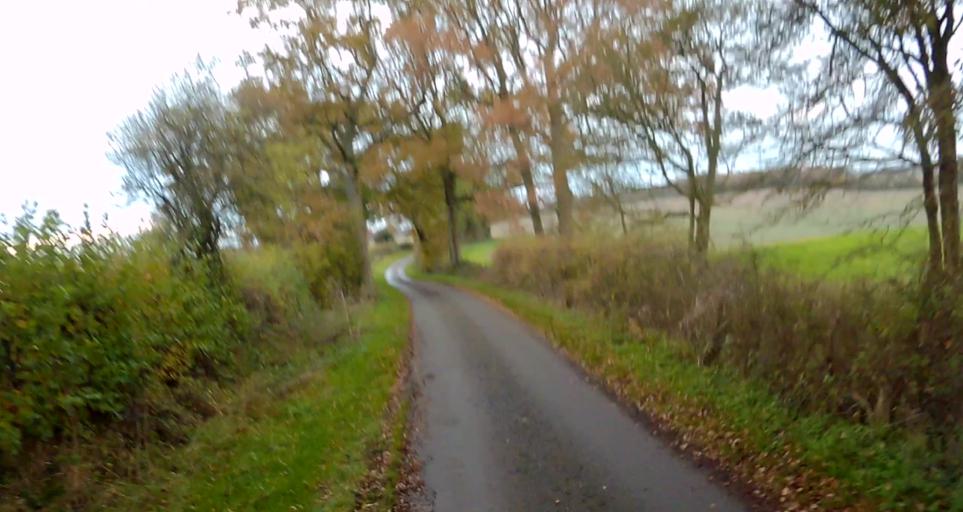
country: GB
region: England
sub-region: Hampshire
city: Long Sutton
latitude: 51.2333
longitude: -0.9059
